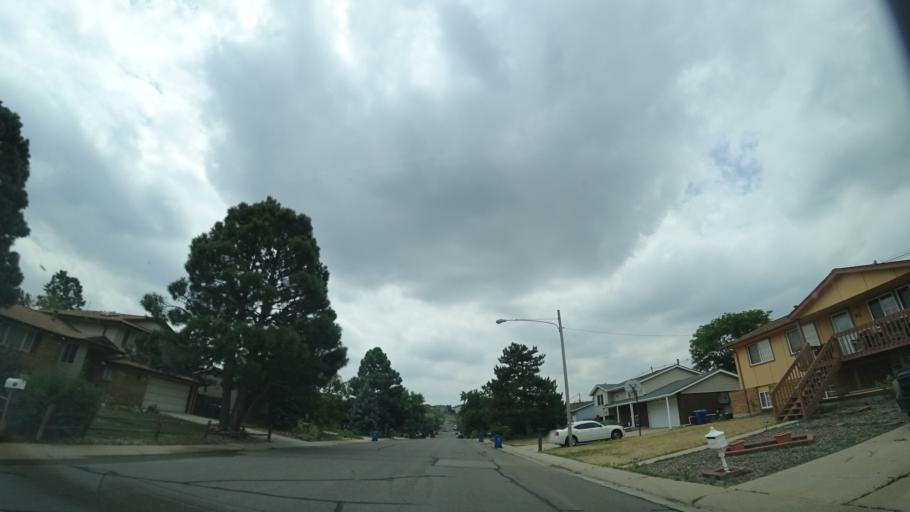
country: US
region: Colorado
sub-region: Jefferson County
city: West Pleasant View
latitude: 39.7156
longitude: -105.1470
